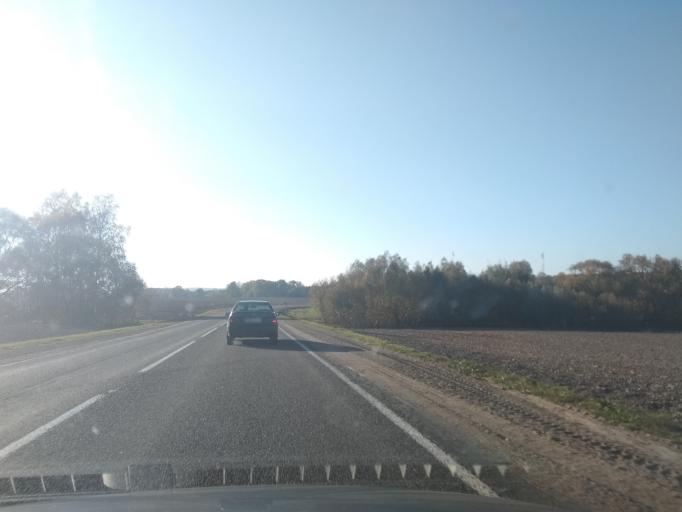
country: BY
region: Grodnenskaya
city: Vyalikaya Byerastavitsa
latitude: 53.1173
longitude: 23.9287
